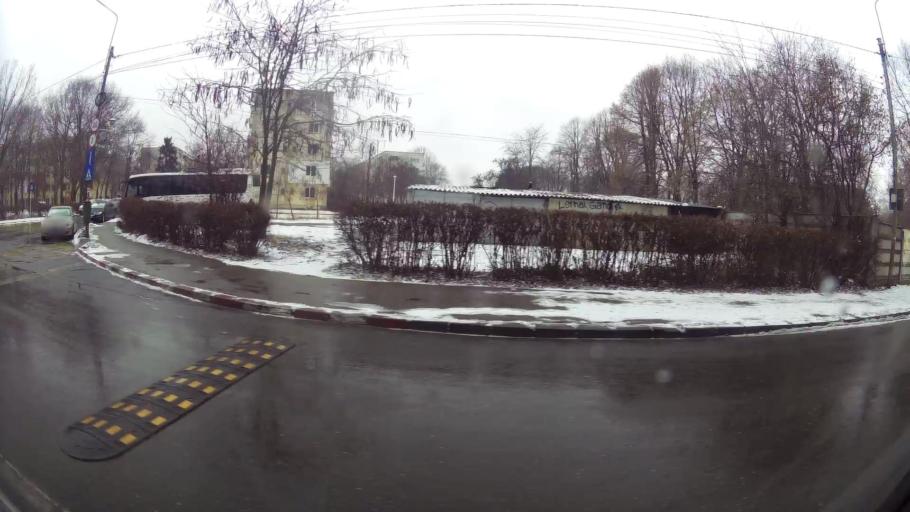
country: RO
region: Prahova
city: Ploiesti
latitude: 44.9558
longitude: 26.0092
